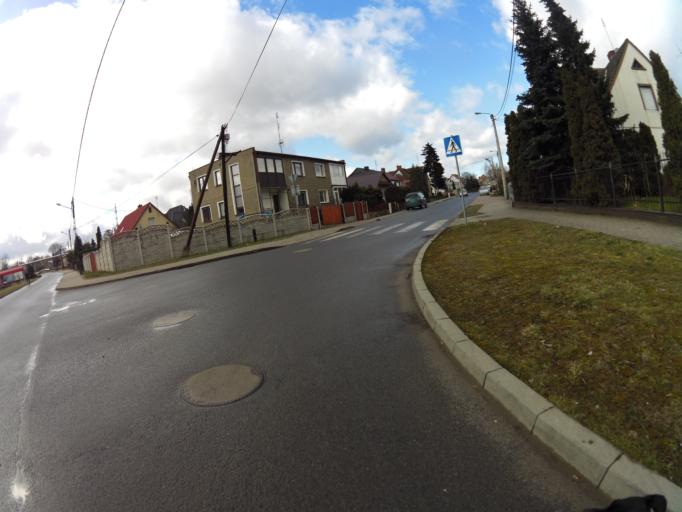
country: PL
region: West Pomeranian Voivodeship
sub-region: Powiat mysliborski
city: Debno
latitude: 52.7336
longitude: 14.7133
